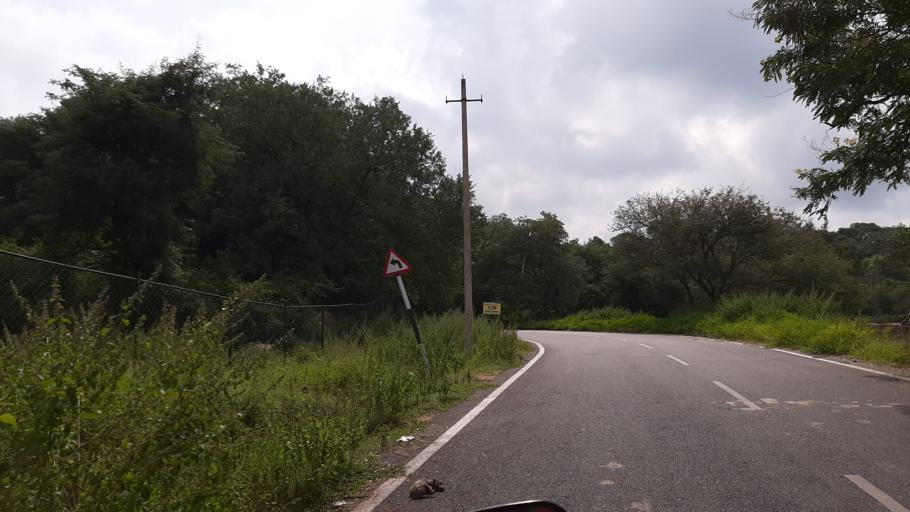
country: IN
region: Karnataka
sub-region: Ramanagara
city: Magadi
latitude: 12.9069
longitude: 77.2933
